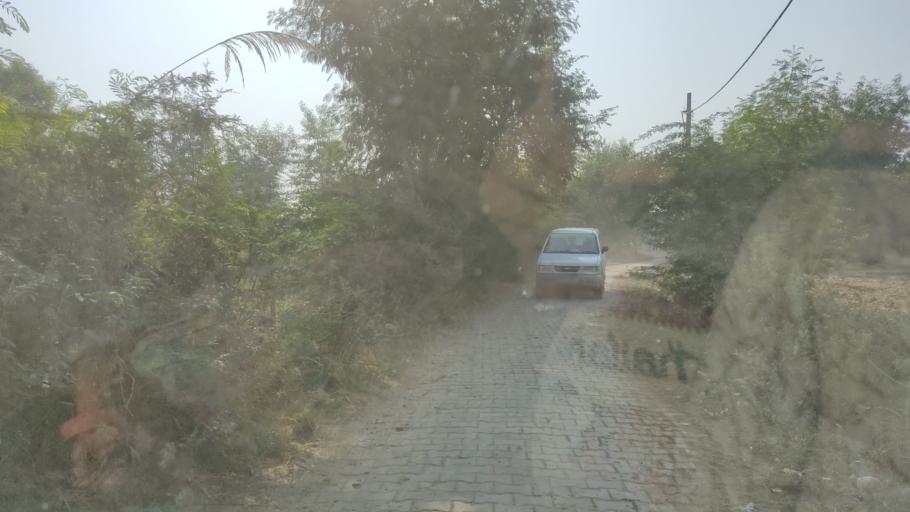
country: IN
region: Uttar Pradesh
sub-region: Mathura
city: Radha Kund
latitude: 27.5621
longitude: 77.5574
